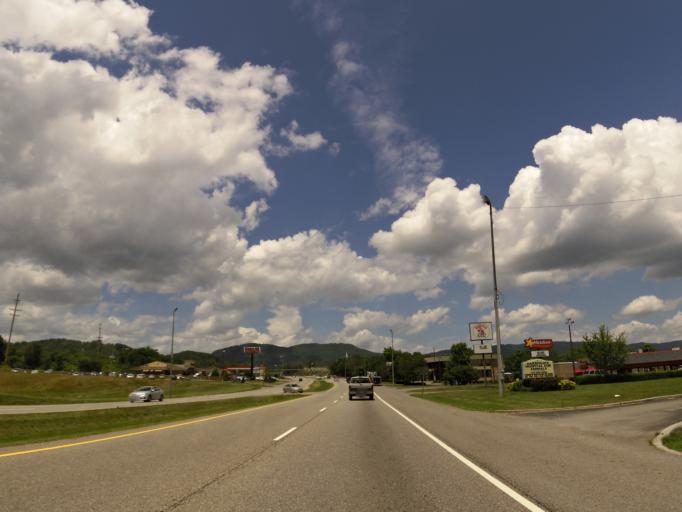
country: US
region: Tennessee
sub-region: Claiborne County
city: Harrogate
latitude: 36.5717
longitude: -83.6536
